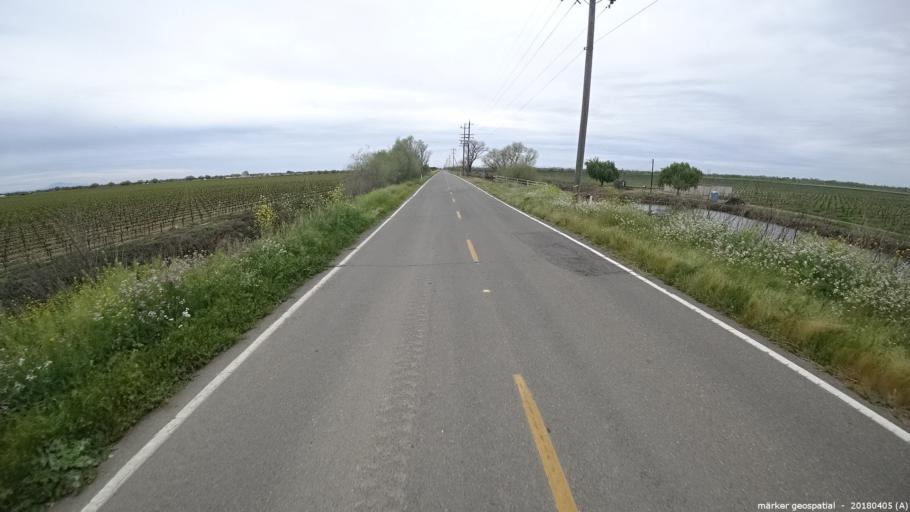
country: US
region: California
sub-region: Sacramento County
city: Walnut Grove
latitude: 38.3205
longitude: -121.4774
